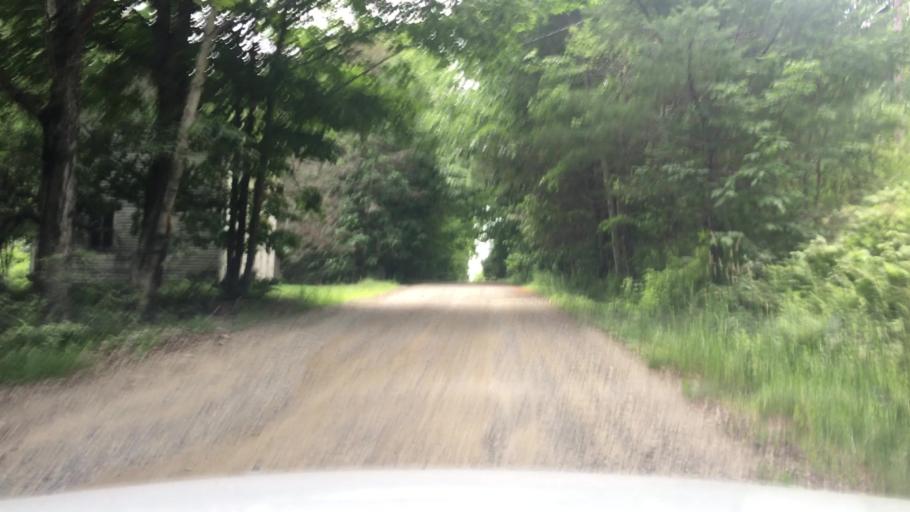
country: US
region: Maine
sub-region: Waldo County
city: Searsmont
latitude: 44.4408
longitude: -69.2506
